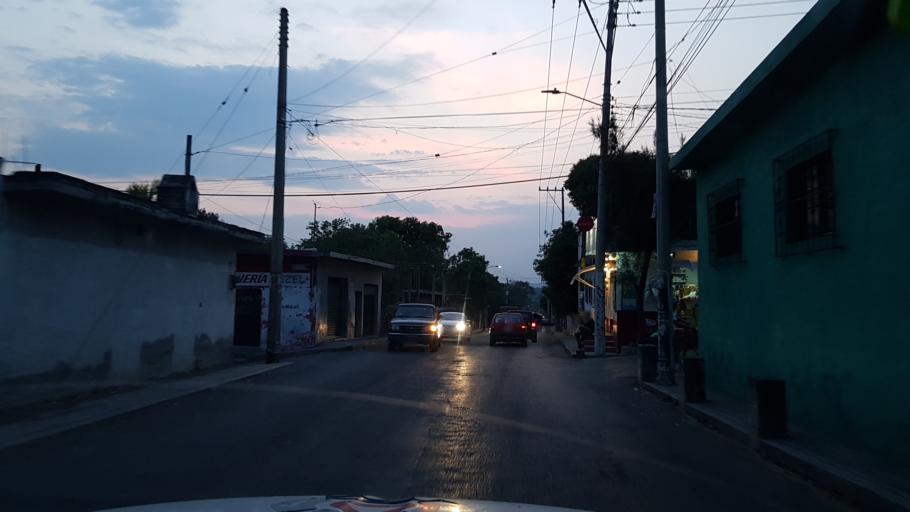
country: MX
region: Morelos
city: Tlaltizapan
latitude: 18.6877
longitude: -99.1198
